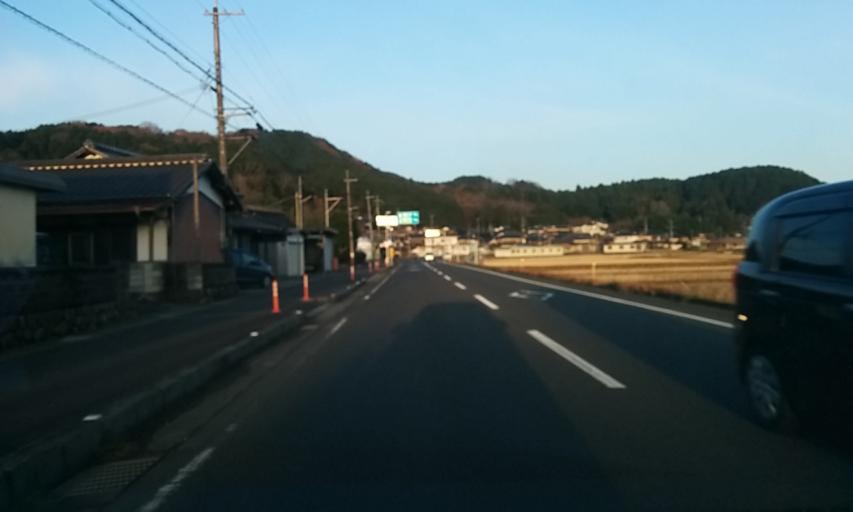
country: JP
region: Kyoto
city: Ayabe
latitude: 35.3137
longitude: 135.2230
